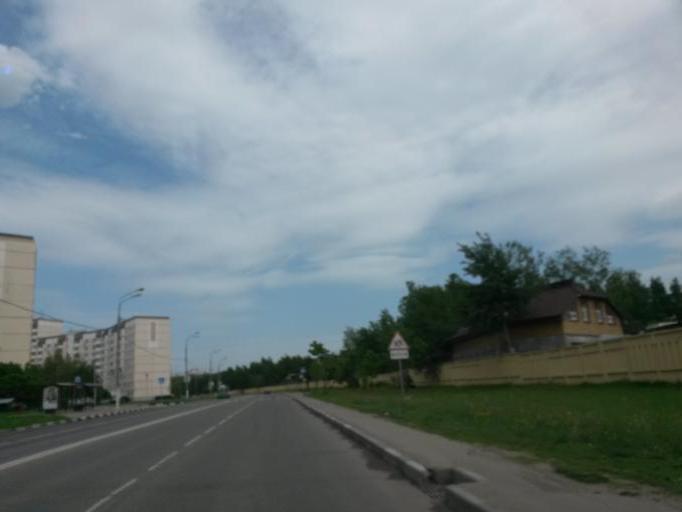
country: RU
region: Moskovskaya
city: Shcherbinka
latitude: 55.5362
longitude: 37.5408
